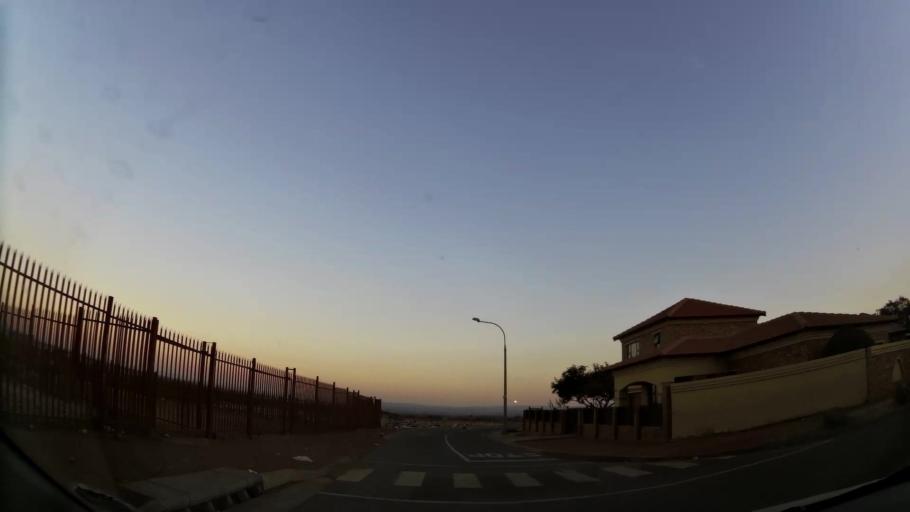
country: ZA
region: Gauteng
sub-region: West Rand District Municipality
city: Randfontein
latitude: -26.2059
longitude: 27.7166
